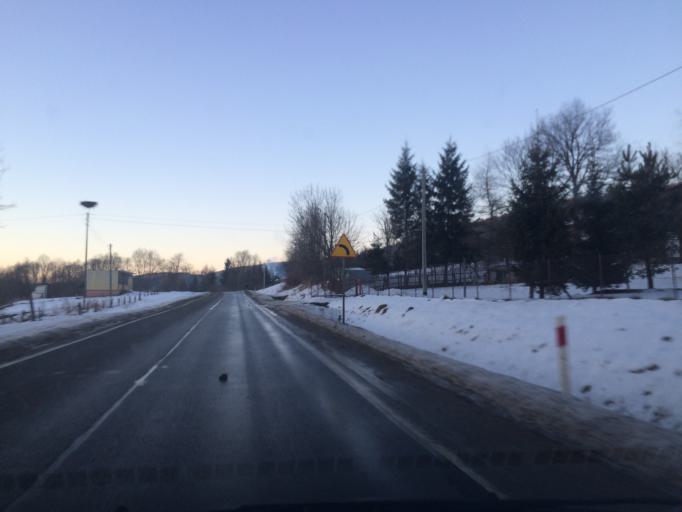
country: PL
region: Subcarpathian Voivodeship
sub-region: Powiat bieszczadzki
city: Czarna
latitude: 49.3753
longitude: 22.6454
